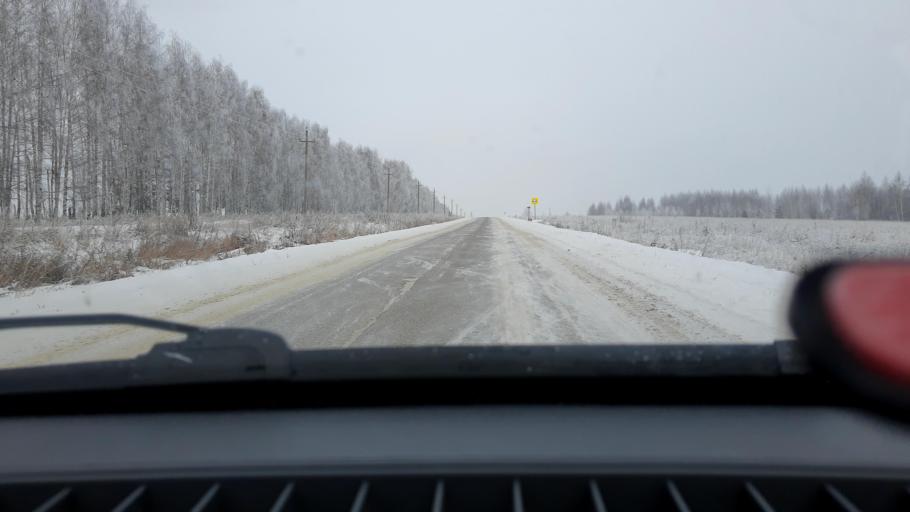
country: RU
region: Bashkortostan
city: Iglino
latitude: 54.6533
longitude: 56.4262
